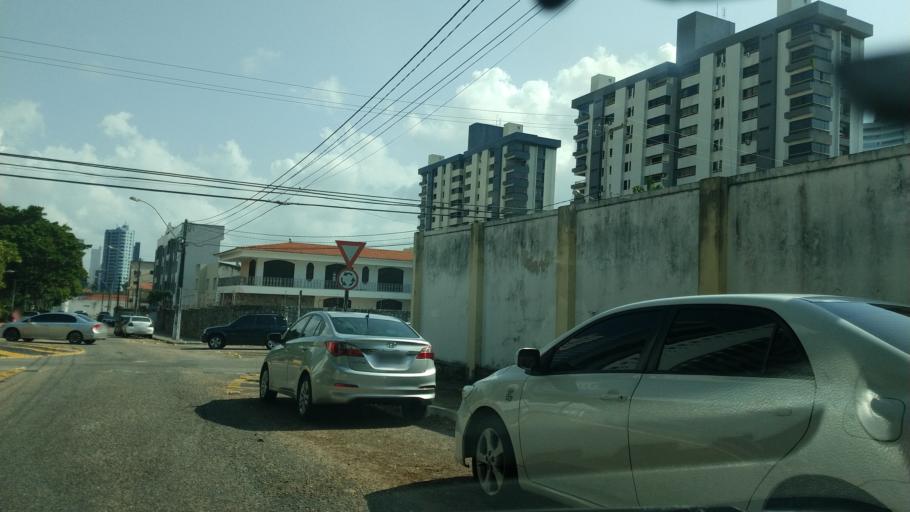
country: BR
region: Rio Grande do Norte
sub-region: Natal
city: Natal
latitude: -5.7926
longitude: -35.2017
